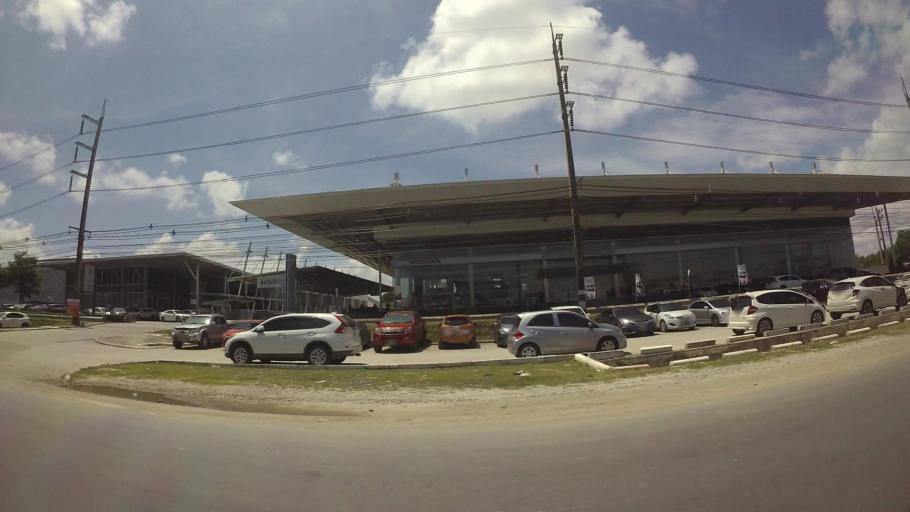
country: TH
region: Rayong
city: Rayong
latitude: 12.6991
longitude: 101.2561
